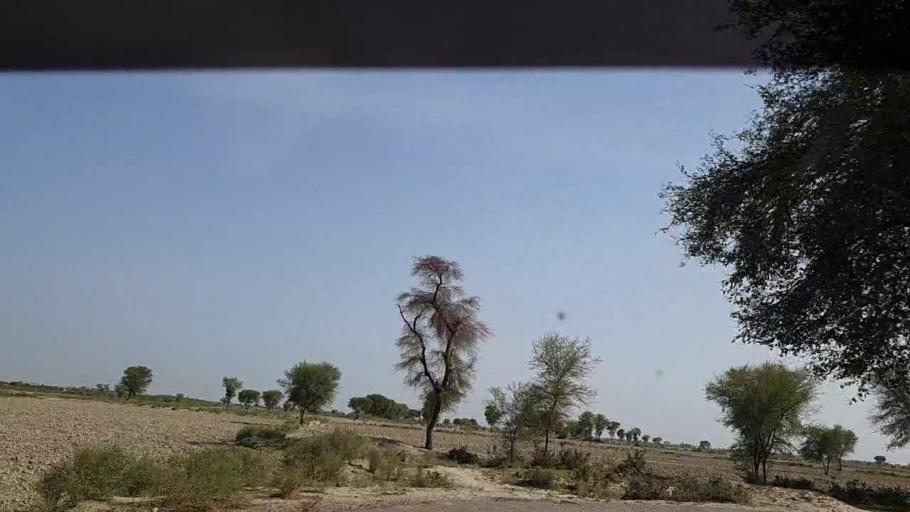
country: PK
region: Sindh
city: Phulji
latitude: 26.9247
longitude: 67.6818
